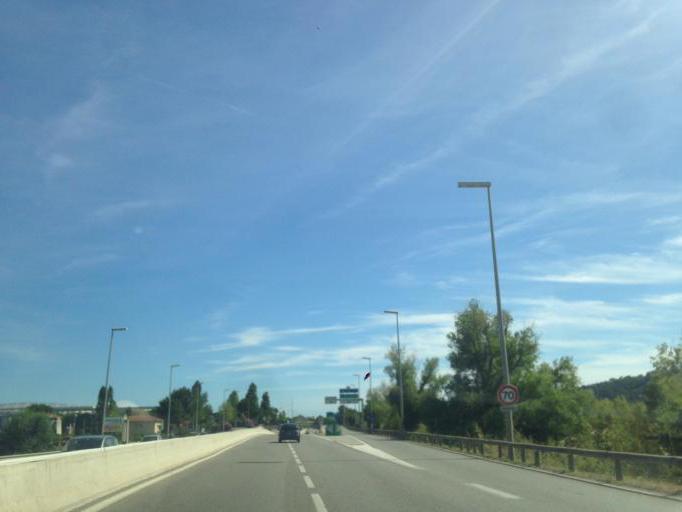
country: FR
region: Provence-Alpes-Cote d'Azur
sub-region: Departement des Alpes-Maritimes
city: La Gaude
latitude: 43.7126
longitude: 7.1873
